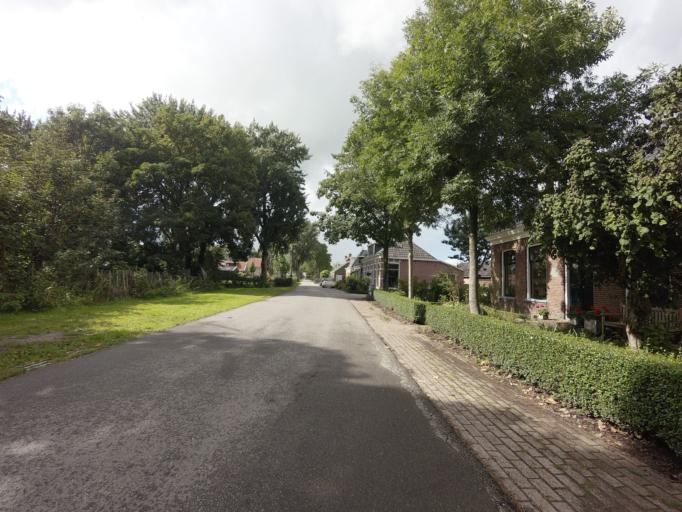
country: NL
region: Friesland
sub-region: Gemeente Boarnsterhim
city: Wergea
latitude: 53.1524
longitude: 5.8401
